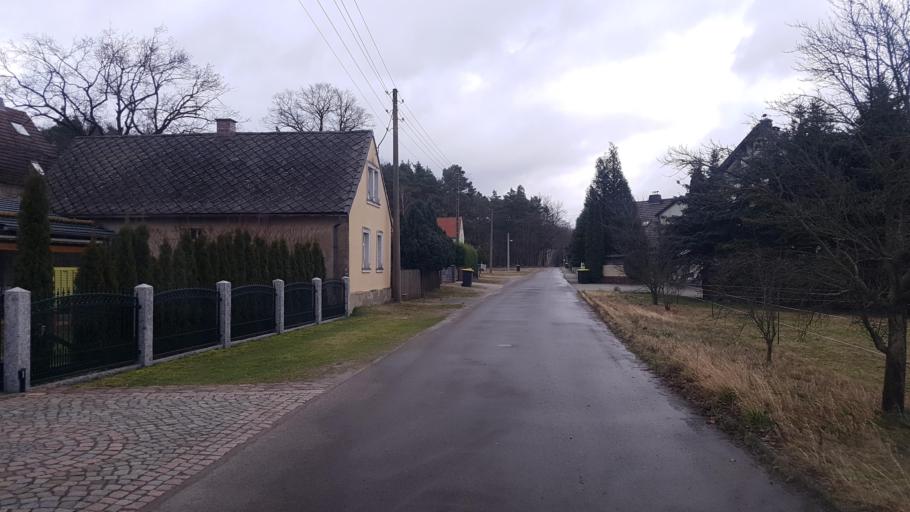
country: DE
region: Brandenburg
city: Kroppen
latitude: 51.3785
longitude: 13.8027
